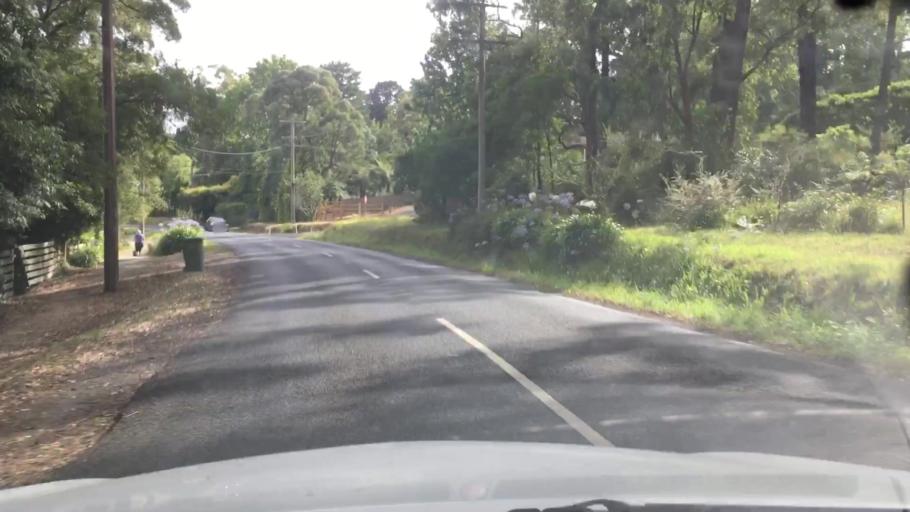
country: AU
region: Victoria
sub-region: Cardinia
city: Cockatoo
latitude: -37.9197
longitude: 145.4688
